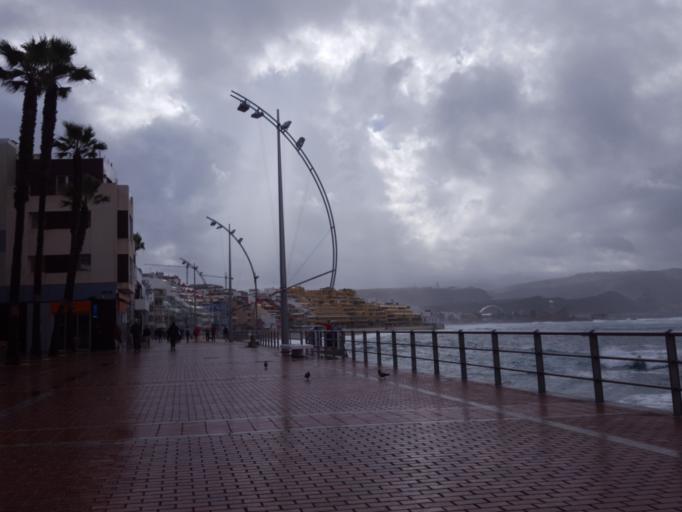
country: ES
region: Canary Islands
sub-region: Provincia de Las Palmas
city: Las Palmas de Gran Canaria
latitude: 28.1395
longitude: -15.4363
